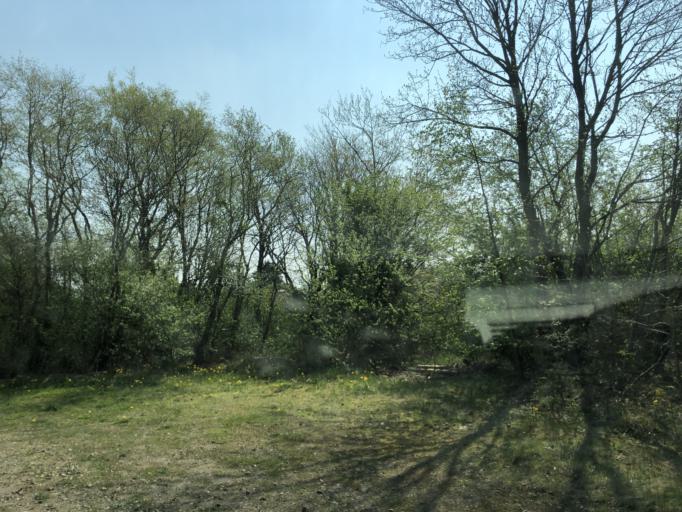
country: DK
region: Central Jutland
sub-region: Holstebro Kommune
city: Holstebro
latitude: 56.3303
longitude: 8.4840
